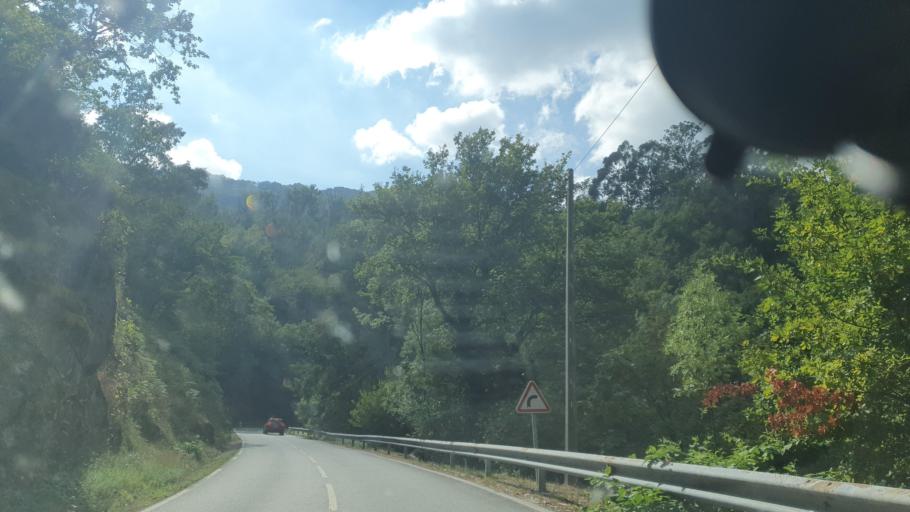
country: PT
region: Braga
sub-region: Vieira do Minho
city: Real
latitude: 41.7047
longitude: -8.2157
